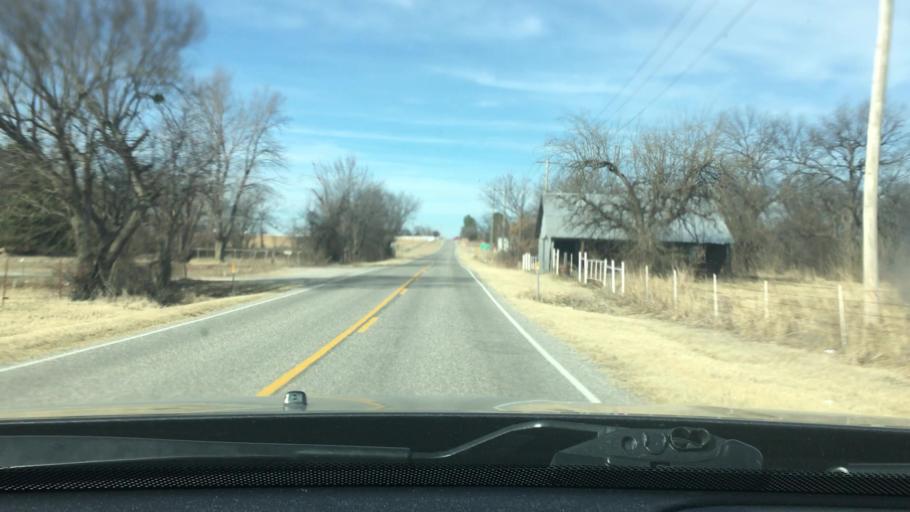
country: US
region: Oklahoma
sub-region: Murray County
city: Davis
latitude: 34.4899
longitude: -97.0905
